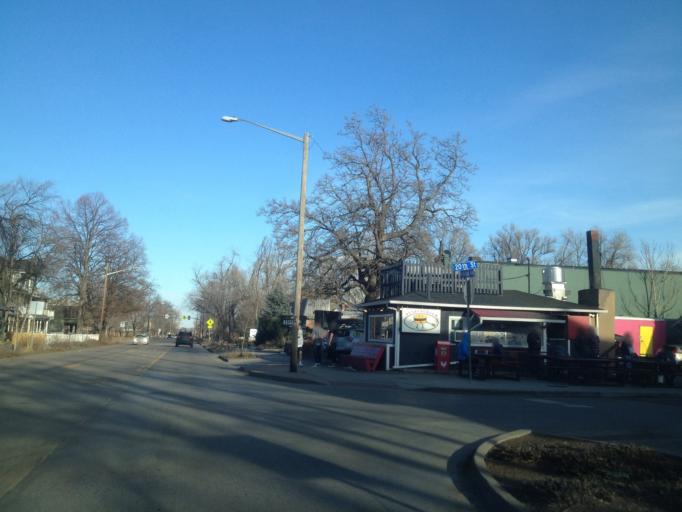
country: US
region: Colorado
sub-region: Boulder County
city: Boulder
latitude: 40.0146
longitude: -105.2692
